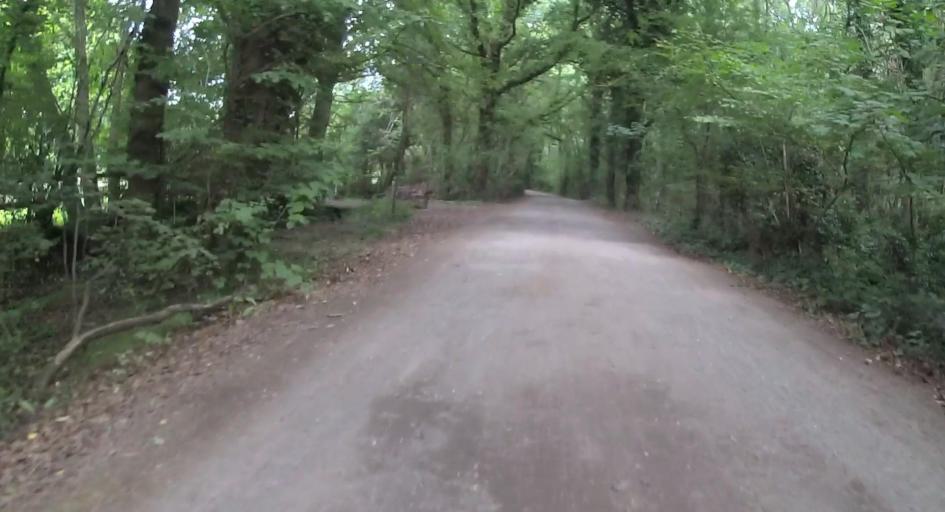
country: GB
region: England
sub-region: Surrey
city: Woking
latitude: 51.3379
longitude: -0.5626
